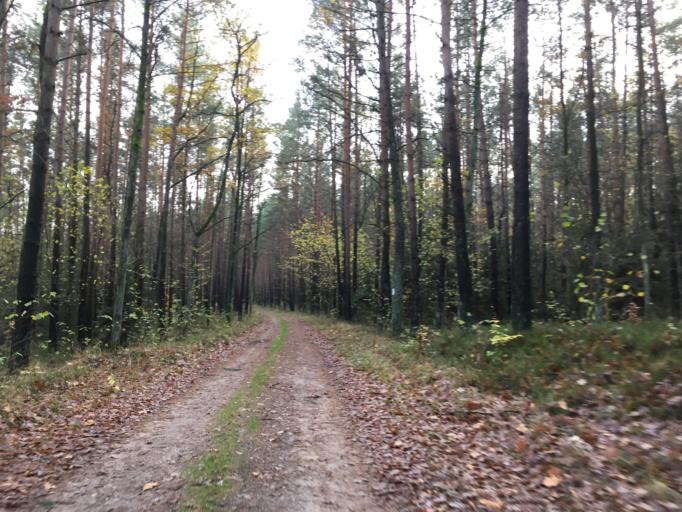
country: PL
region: Kujawsko-Pomorskie
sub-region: Powiat brodnicki
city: Gorzno
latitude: 53.1888
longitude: 19.7381
